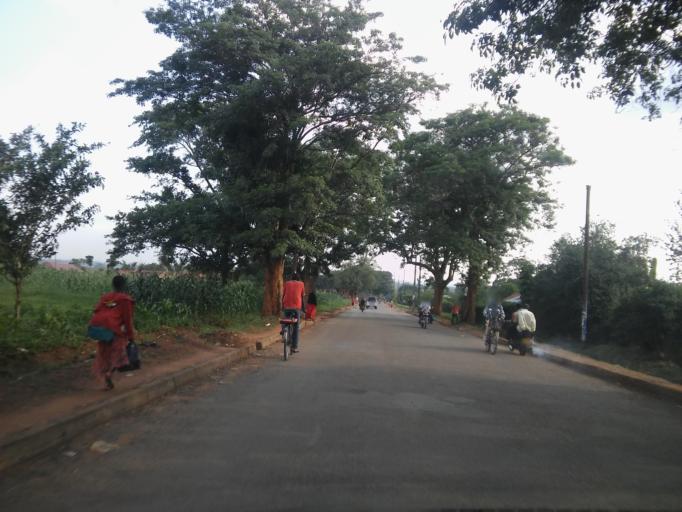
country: UG
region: Eastern Region
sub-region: Mbale District
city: Mbale
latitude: 1.0687
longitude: 34.1822
